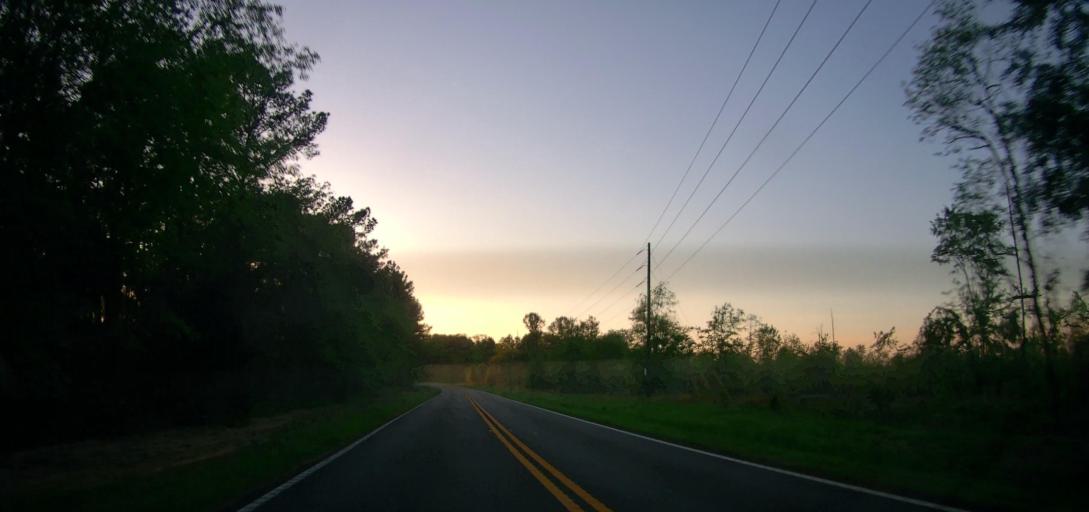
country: US
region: Georgia
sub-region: Marion County
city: Buena Vista
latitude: 32.3686
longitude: -84.5433
